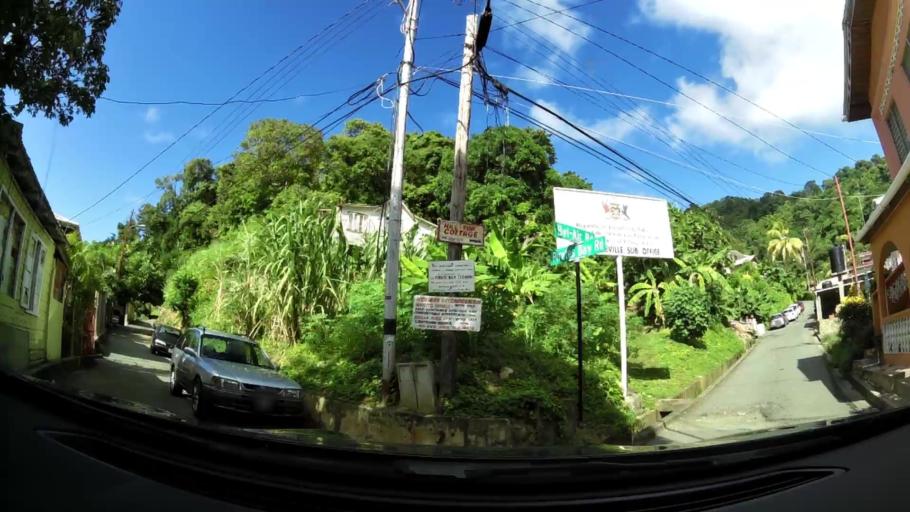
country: TT
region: Eastern Tobago
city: Roxborough
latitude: 11.3247
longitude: -60.5486
